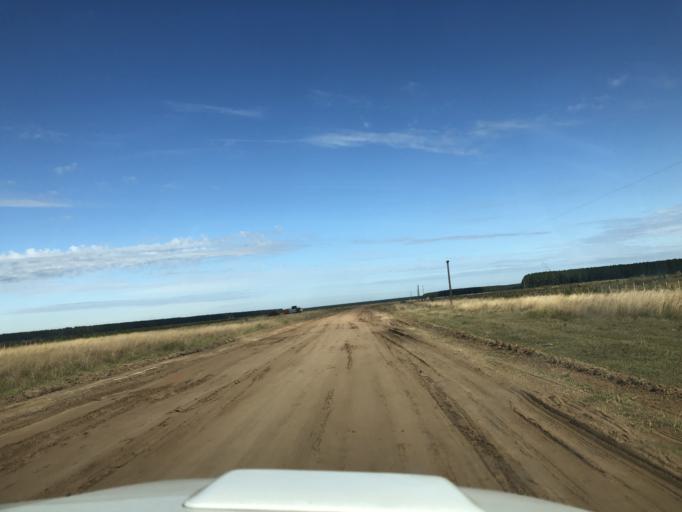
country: AR
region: Corrientes
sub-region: Departamento de Concepcion
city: Concepcion
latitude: -28.5156
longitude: -58.0581
